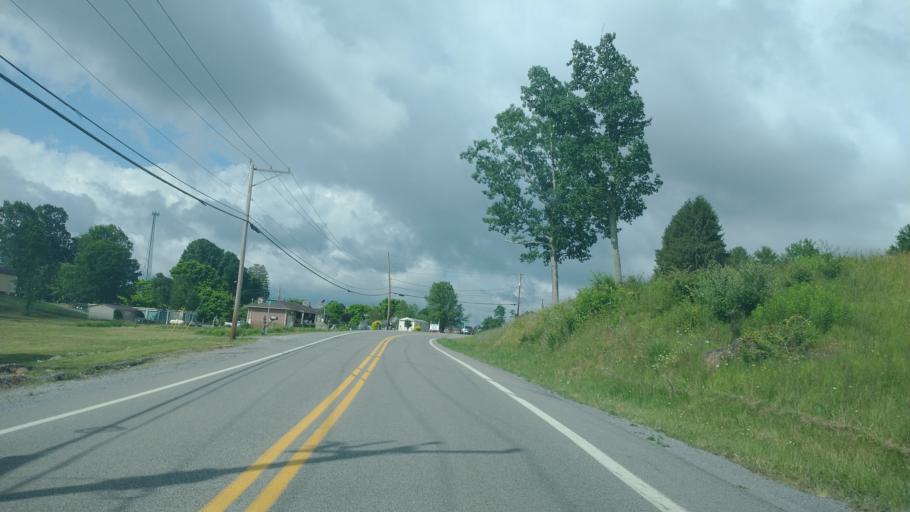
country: US
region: West Virginia
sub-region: Mercer County
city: Princeton
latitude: 37.3571
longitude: -81.1452
